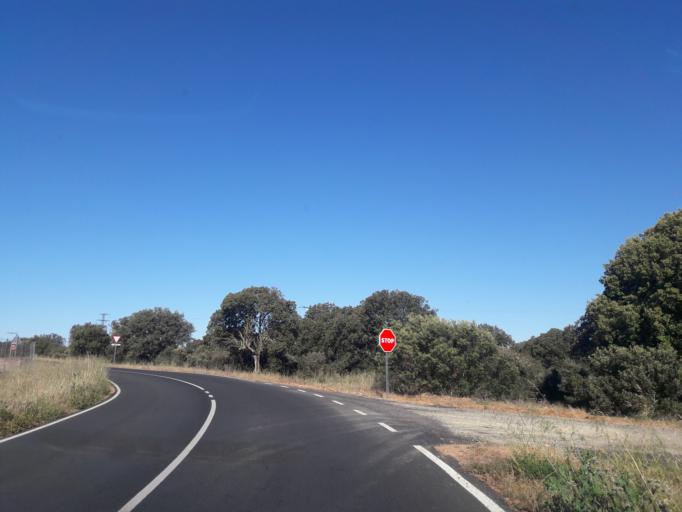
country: ES
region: Castille and Leon
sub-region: Provincia de Salamanca
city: Doninos de Salamanca
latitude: 40.9294
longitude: -5.7375
